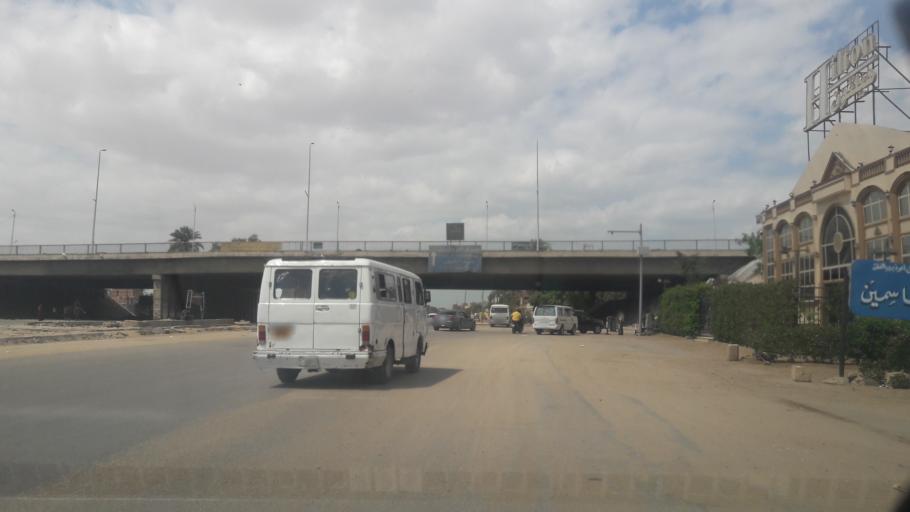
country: EG
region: Al Jizah
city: Al Jizah
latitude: 29.9543
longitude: 31.1550
